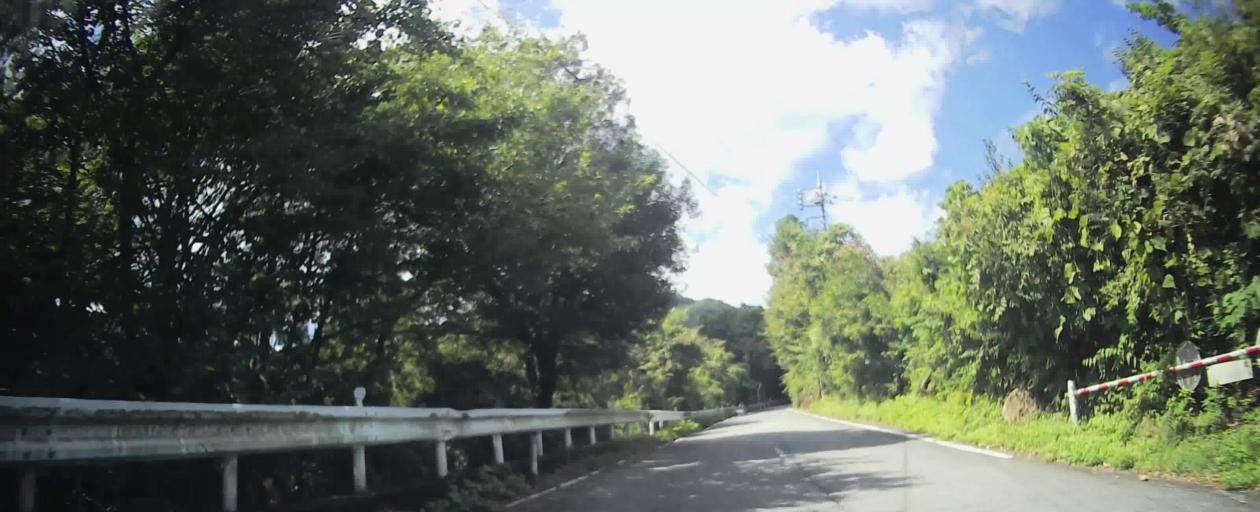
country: JP
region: Gunma
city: Kanekomachi
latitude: 36.4447
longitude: 138.9076
